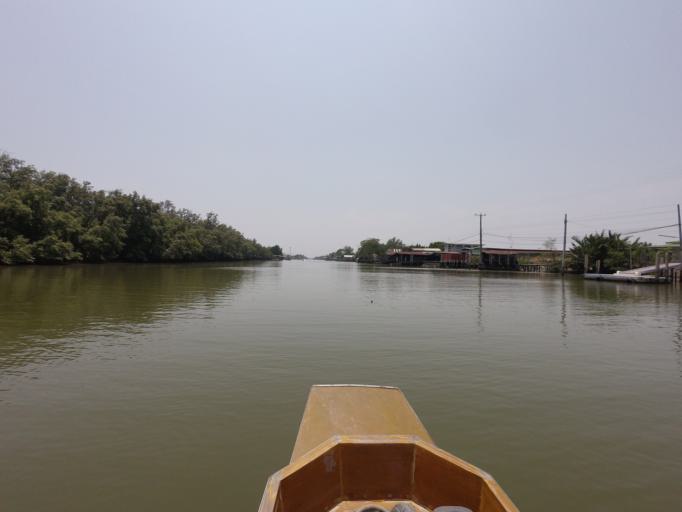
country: TH
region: Bangkok
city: Thung Khru
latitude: 13.5447
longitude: 100.4772
